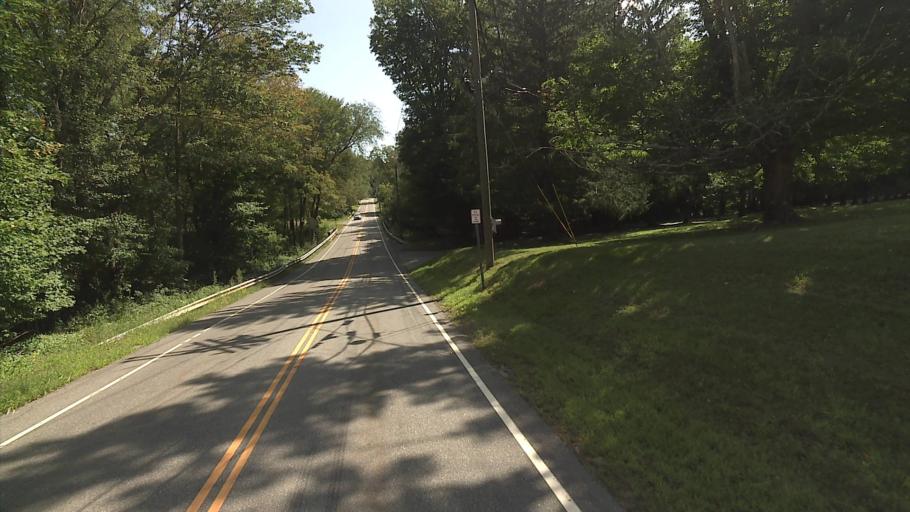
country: US
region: Connecticut
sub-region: New London County
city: Colchester
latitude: 41.6297
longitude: -72.3000
